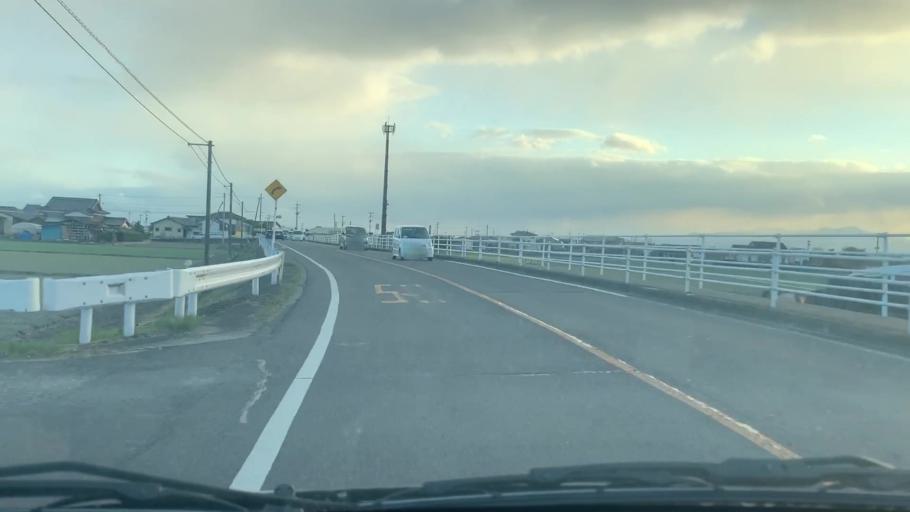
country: JP
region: Saga Prefecture
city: Saga-shi
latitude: 33.1899
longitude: 130.1928
